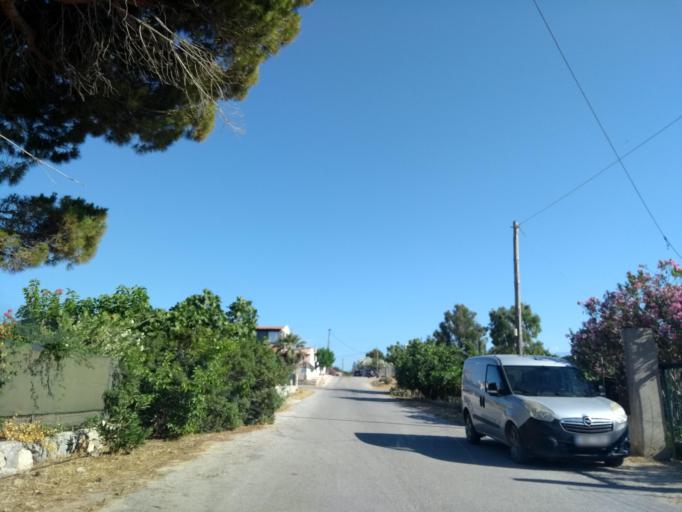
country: GR
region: Crete
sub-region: Nomos Chanias
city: Pithari
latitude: 35.5892
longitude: 24.0916
